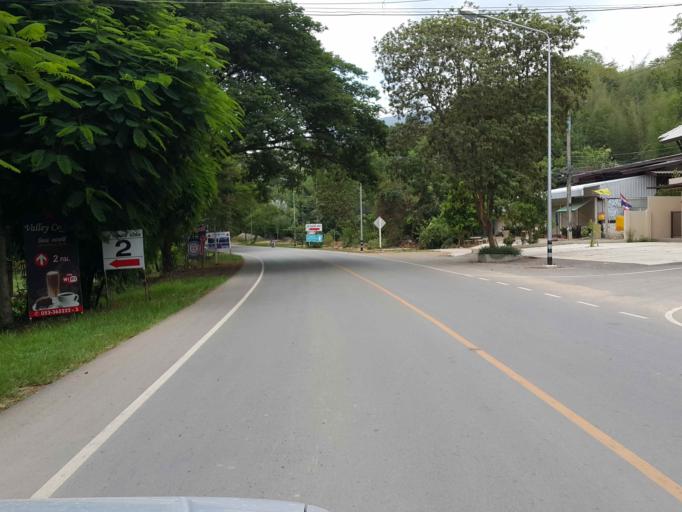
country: TH
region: Chiang Mai
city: Hang Dong
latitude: 18.7485
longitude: 98.8903
